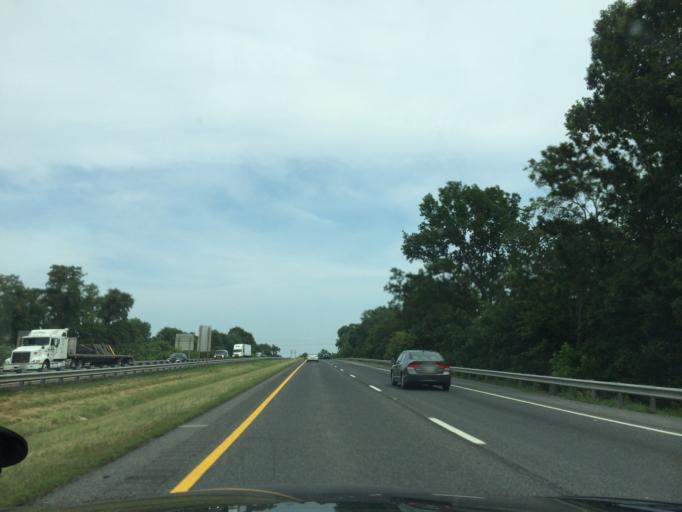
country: US
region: Maryland
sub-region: Washington County
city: Williamsport
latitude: 39.6242
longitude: -77.7955
